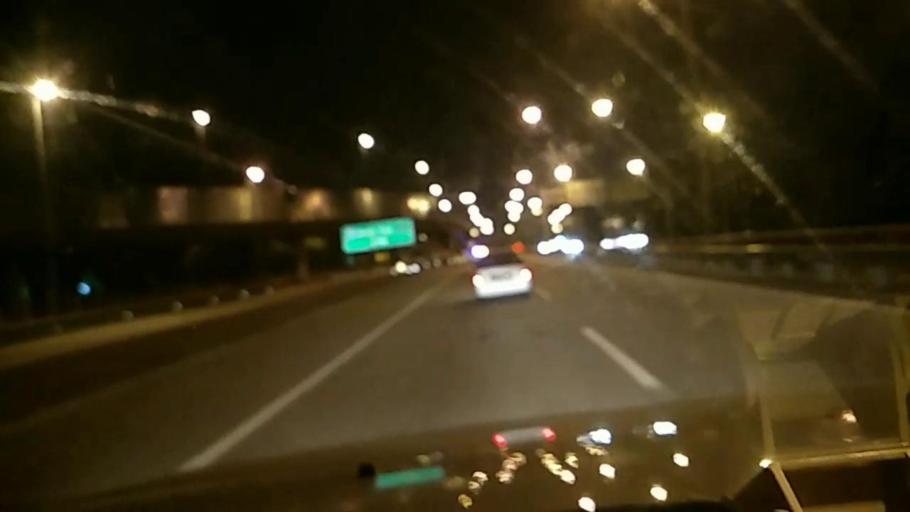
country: MY
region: Penang
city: Perai
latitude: 5.3613
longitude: 100.4040
